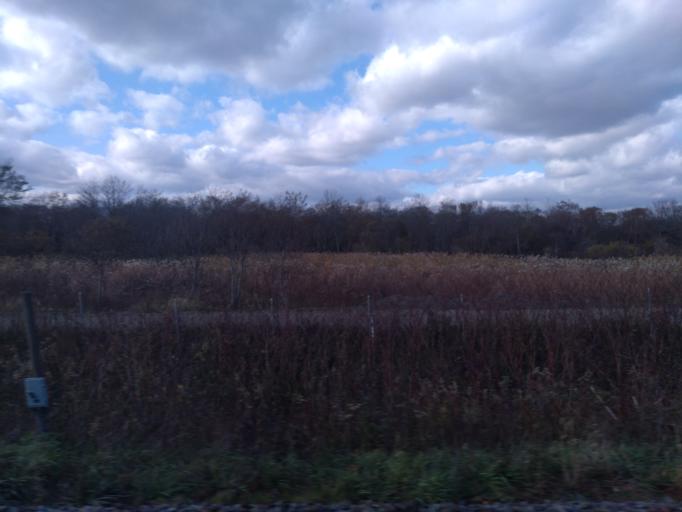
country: JP
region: Hokkaido
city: Shiraoi
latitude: 42.5045
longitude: 141.2790
